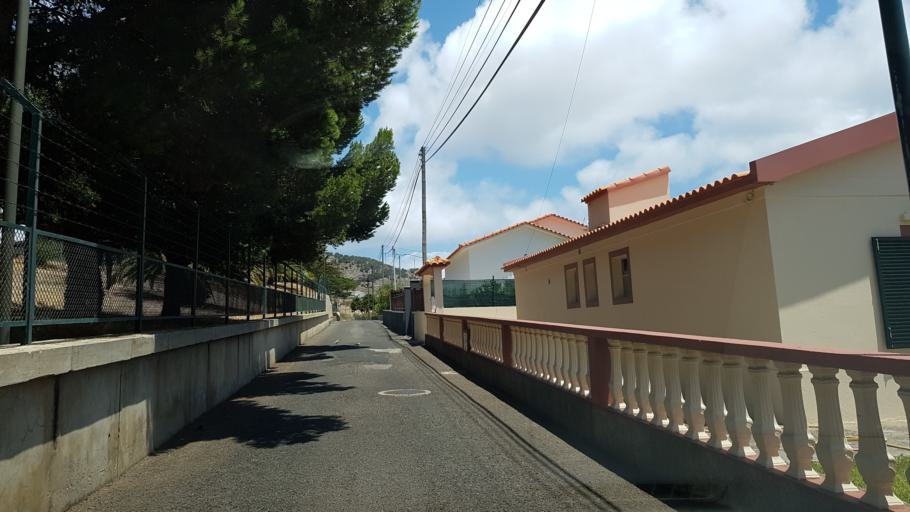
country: PT
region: Madeira
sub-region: Porto Santo
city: Vila de Porto Santo
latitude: 33.0715
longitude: -16.3392
